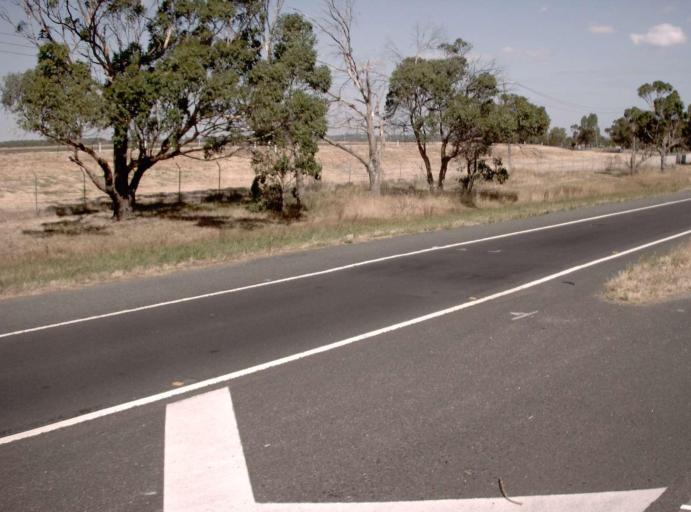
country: AU
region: Victoria
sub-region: Kingston
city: Patterson Lakes
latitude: -38.0632
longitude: 145.1491
